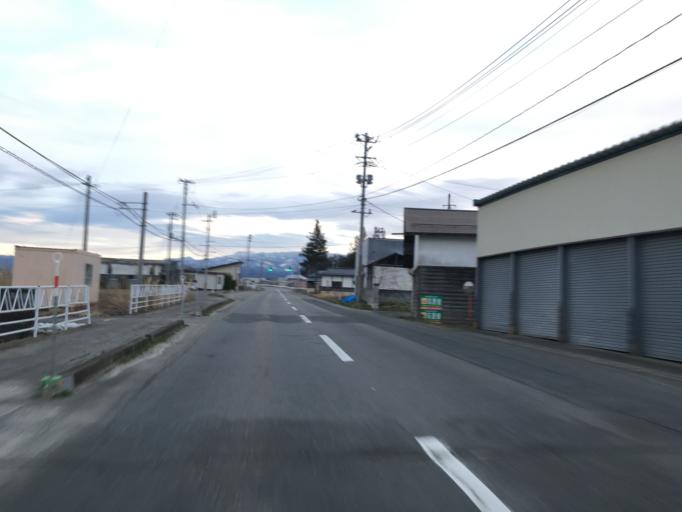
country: JP
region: Yamagata
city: Yonezawa
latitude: 37.9516
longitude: 140.0690
